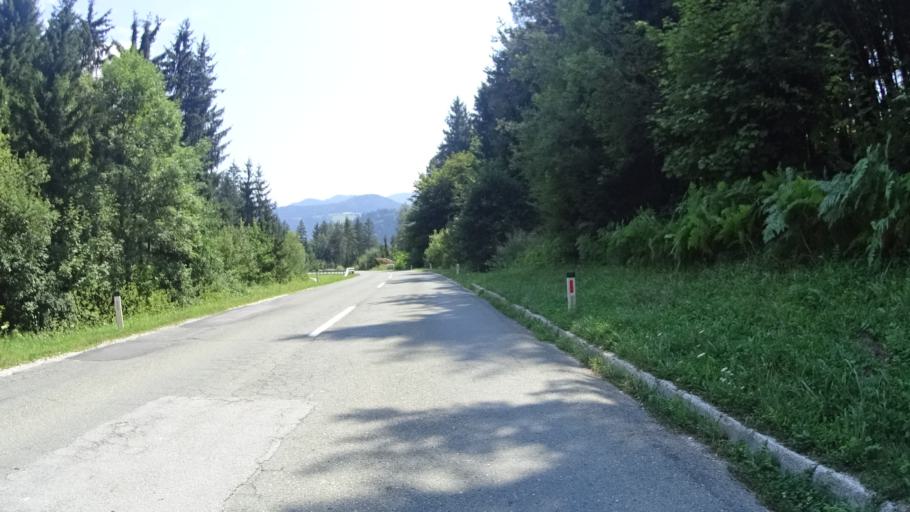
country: SI
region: Mezica
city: Mezica
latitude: 46.5591
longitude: 14.8493
